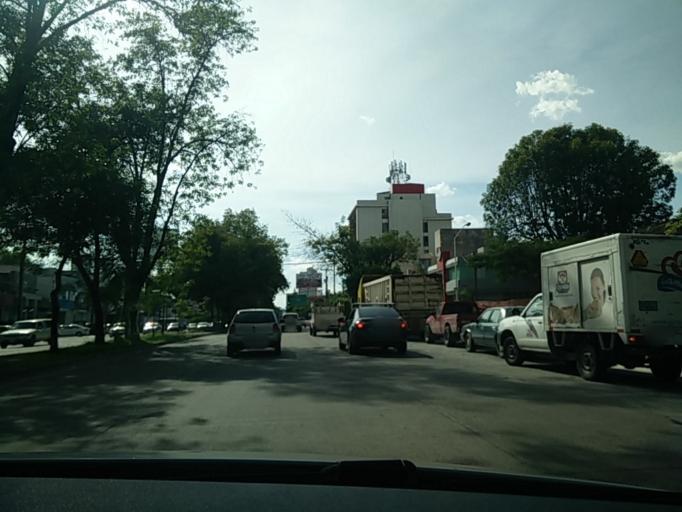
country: MX
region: Jalisco
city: Guadalajara
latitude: 20.6796
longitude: -103.3822
